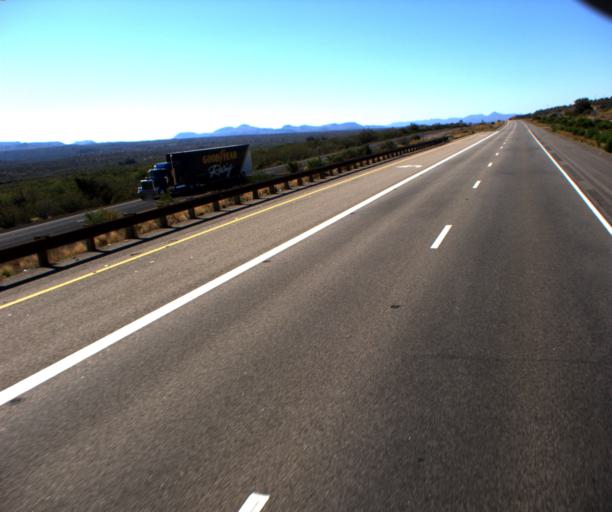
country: US
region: Arizona
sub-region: Yavapai County
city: Bagdad
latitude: 34.8407
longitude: -113.6347
